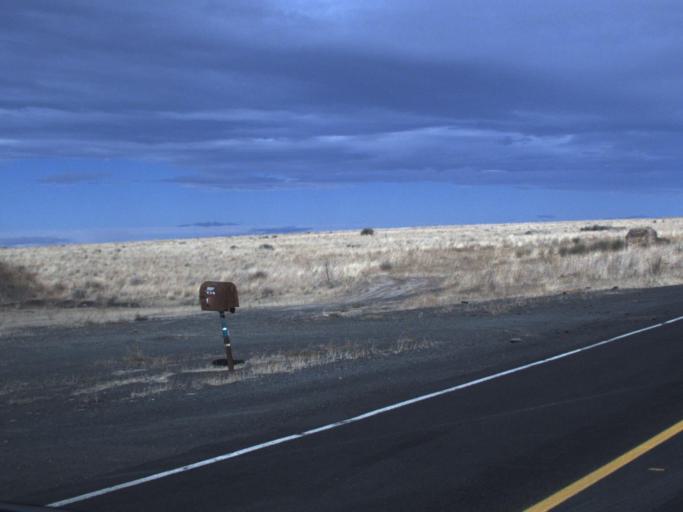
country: US
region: Washington
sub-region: Adams County
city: Ritzville
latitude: 47.3131
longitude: -118.6904
